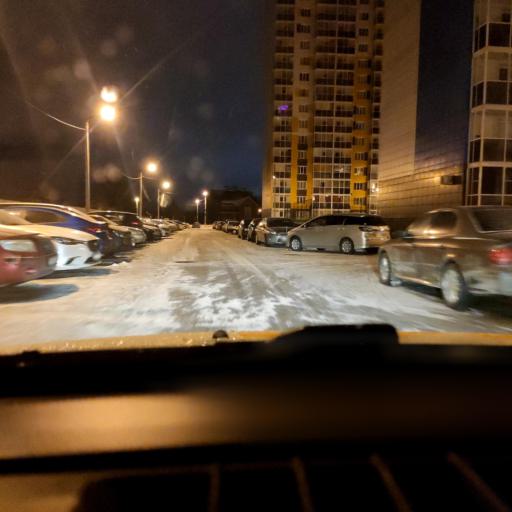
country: RU
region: Voronezj
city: Podgornoye
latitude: 51.7598
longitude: 39.1797
